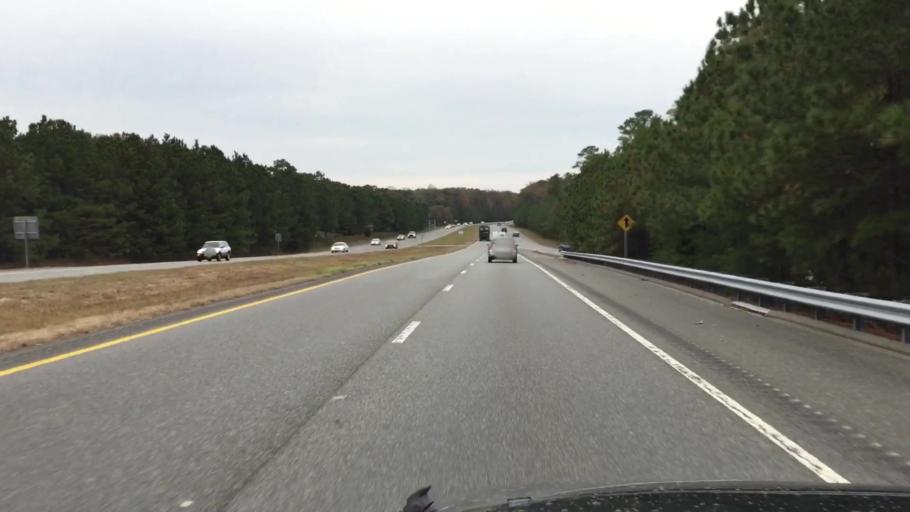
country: US
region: Virginia
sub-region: James City County
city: Williamsburg
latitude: 37.2749
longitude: -76.7524
